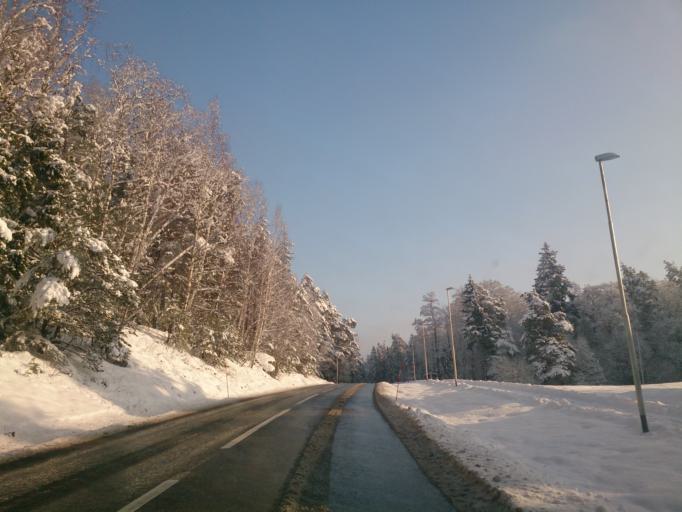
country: SE
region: Stockholm
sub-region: Varmdo Kommun
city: Hemmesta
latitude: 59.2825
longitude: 18.5689
